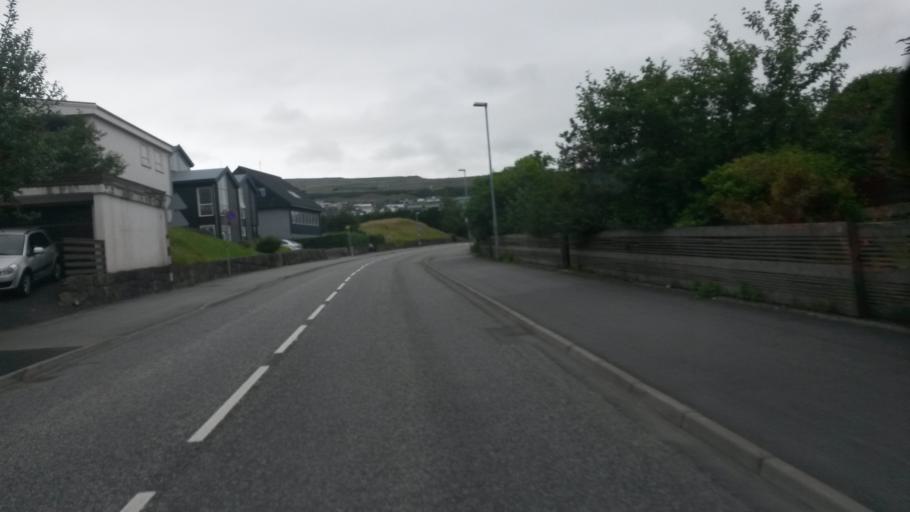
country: FO
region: Streymoy
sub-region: Torshavn
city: Torshavn
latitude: 62.0056
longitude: -6.7832
